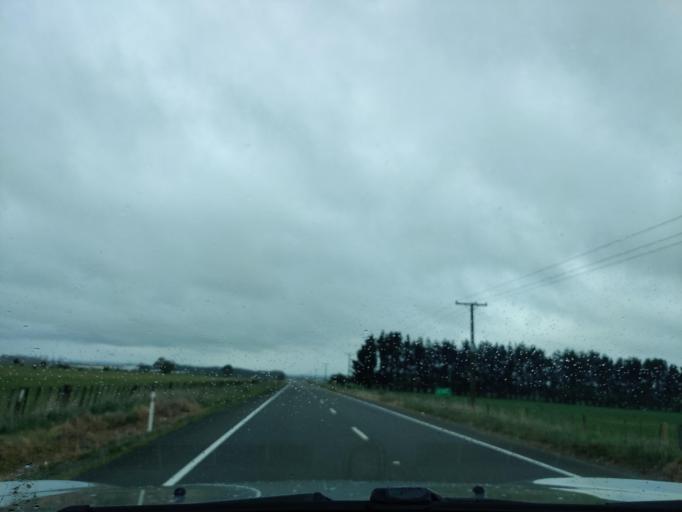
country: NZ
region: Hawke's Bay
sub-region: Hastings District
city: Hastings
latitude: -40.0132
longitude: 176.3670
